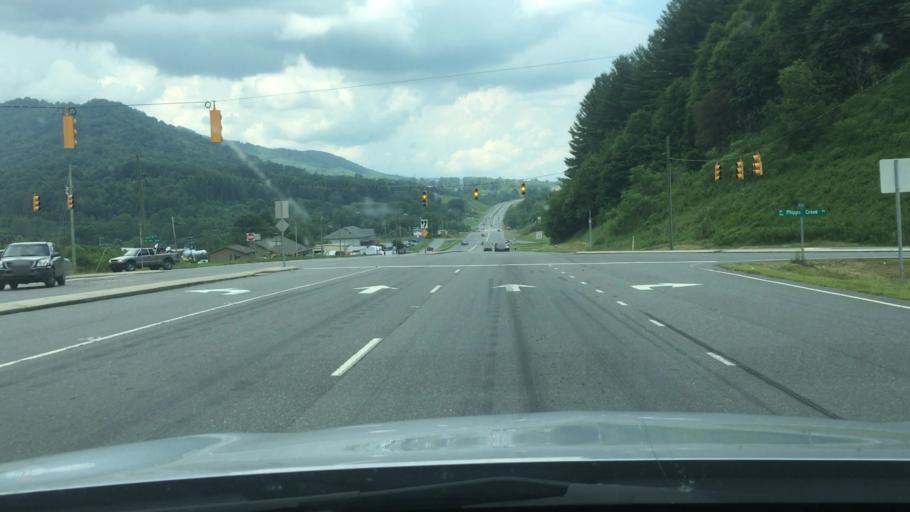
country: US
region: North Carolina
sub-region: Yancey County
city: Burnsville
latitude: 35.9102
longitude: -82.3582
